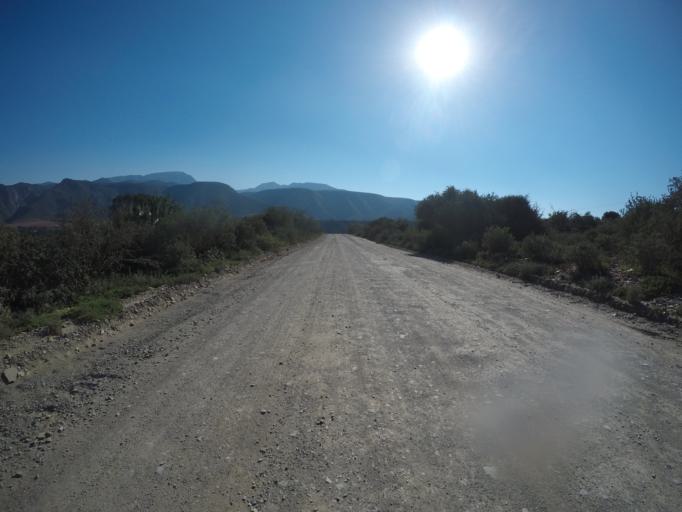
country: ZA
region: Eastern Cape
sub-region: Cacadu District Municipality
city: Kruisfontein
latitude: -33.6719
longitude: 24.5768
